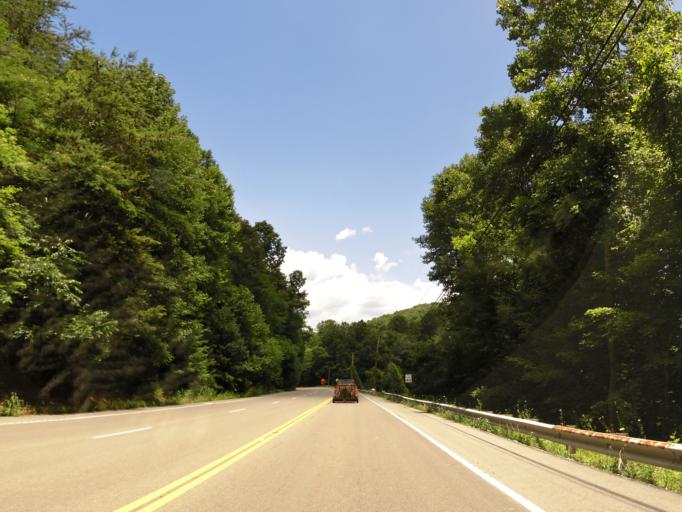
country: US
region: Tennessee
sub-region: Union County
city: Maynardville
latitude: 36.3252
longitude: -83.7473
